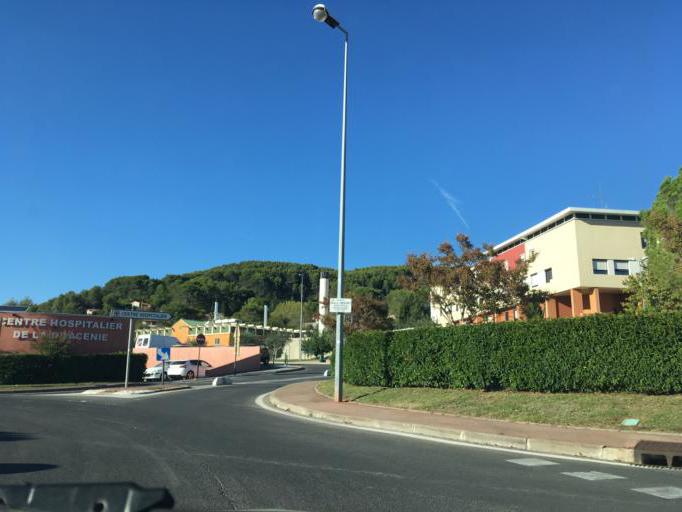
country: FR
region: Provence-Alpes-Cote d'Azur
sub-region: Departement du Var
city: Draguignan
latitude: 43.5483
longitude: 6.4449
